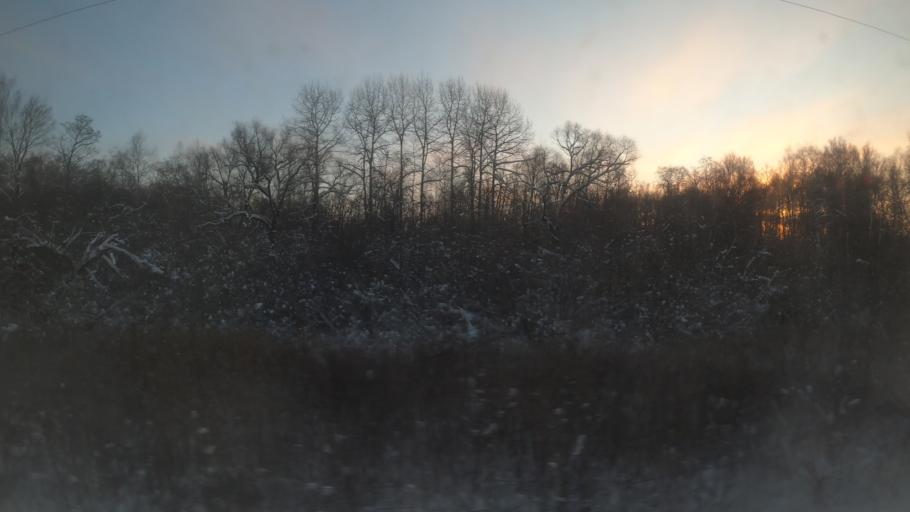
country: RU
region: Moskovskaya
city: Podosinki
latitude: 56.2096
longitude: 37.5265
